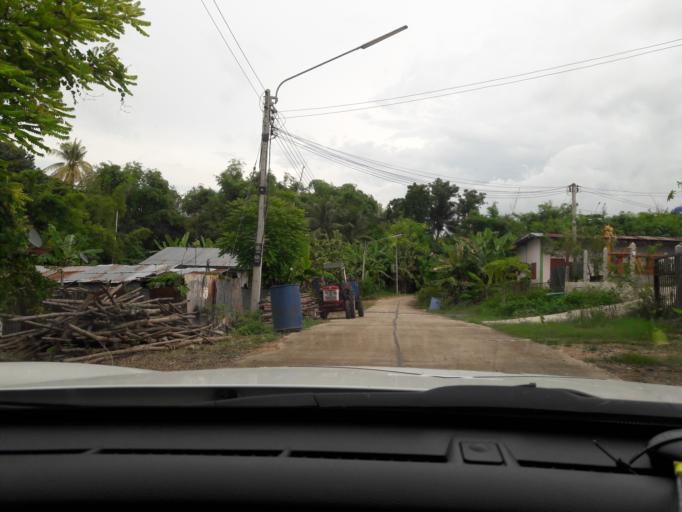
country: TH
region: Nakhon Sawan
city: Tak Fa
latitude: 15.3538
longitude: 100.4969
